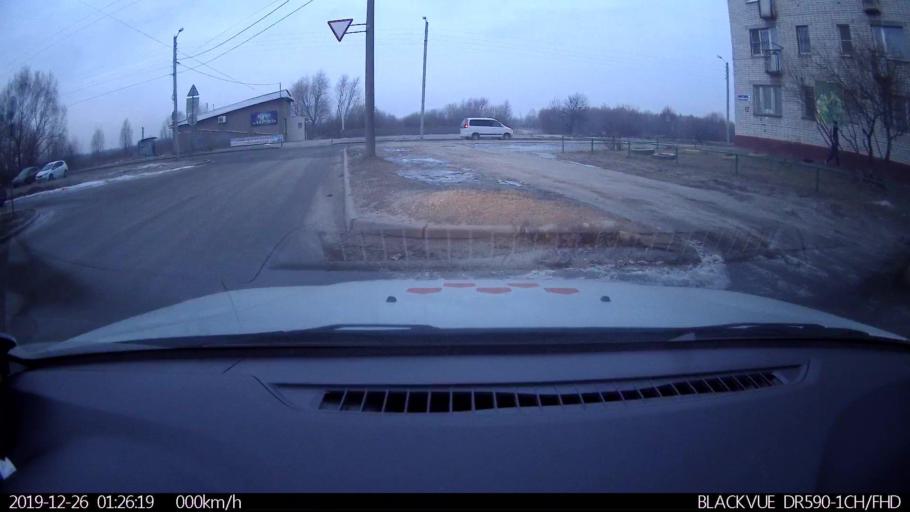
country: RU
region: Nizjnij Novgorod
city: Gorbatovka
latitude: 56.2666
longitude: 43.8631
